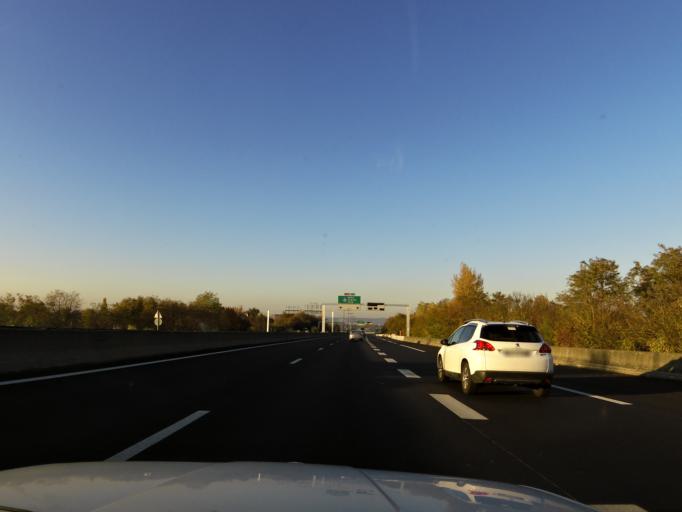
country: FR
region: Rhone-Alpes
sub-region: Departement du Rhone
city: Chassieu
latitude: 45.7530
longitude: 4.9857
